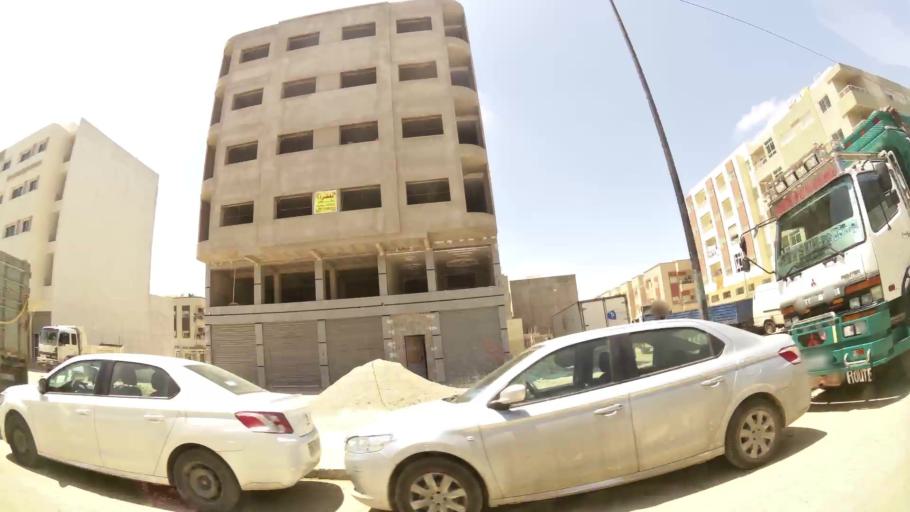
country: MA
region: Fes-Boulemane
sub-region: Fes
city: Fes
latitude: 34.0190
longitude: -5.0533
